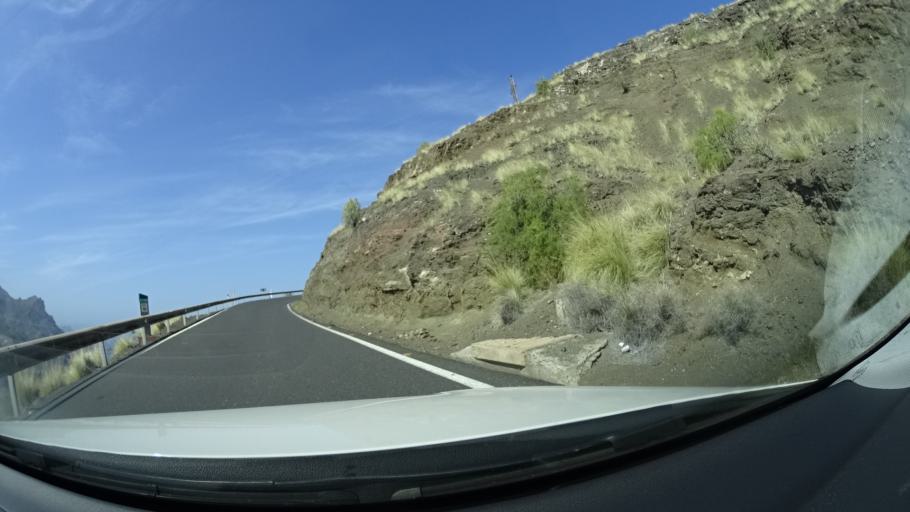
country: ES
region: Canary Islands
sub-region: Provincia de Las Palmas
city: Agaete
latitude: 28.0604
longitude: -15.7302
